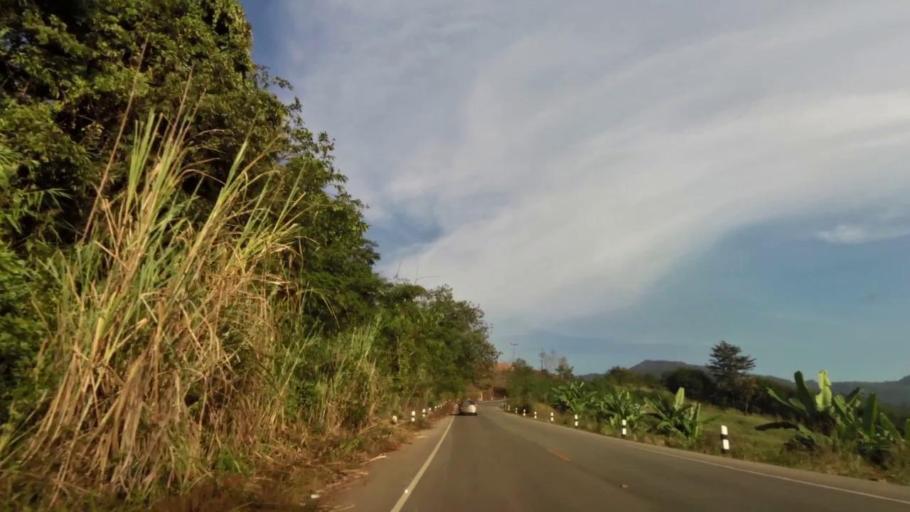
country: TH
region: Chiang Rai
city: Khun Tan
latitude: 19.8671
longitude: 100.4090
